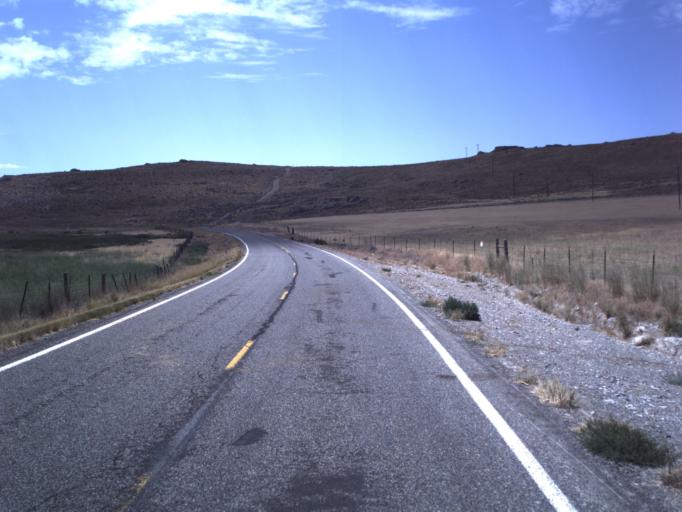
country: US
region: Utah
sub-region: Box Elder County
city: Tremonton
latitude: 41.6195
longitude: -112.3625
